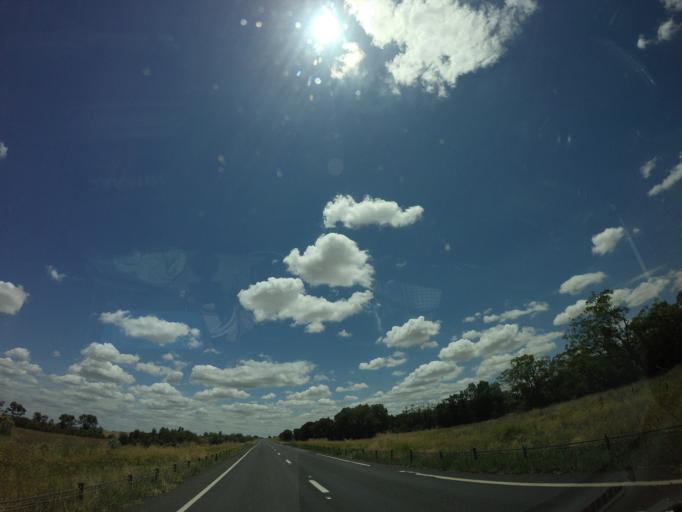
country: AU
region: New South Wales
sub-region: Moree Plains
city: Boggabilla
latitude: -28.7865
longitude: 150.2553
